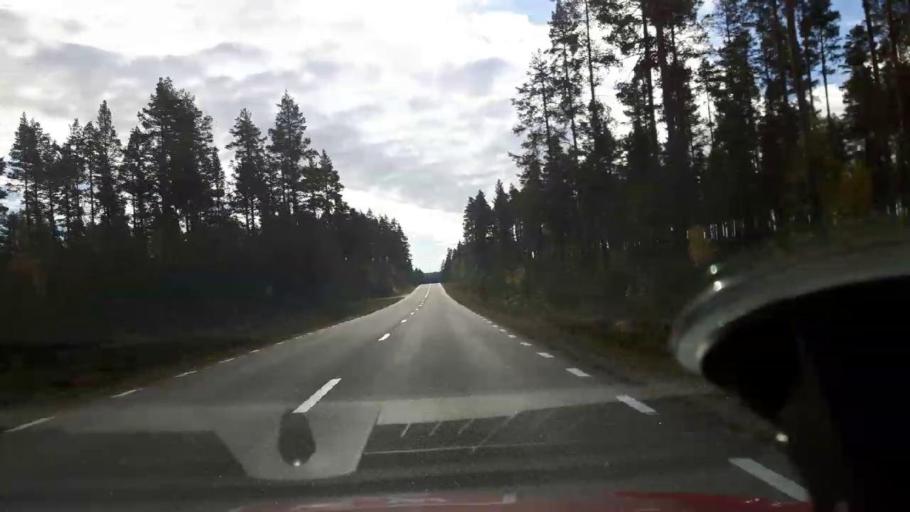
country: SE
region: Gaevleborg
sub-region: Ljusdals Kommun
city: Farila
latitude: 62.0238
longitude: 15.2267
